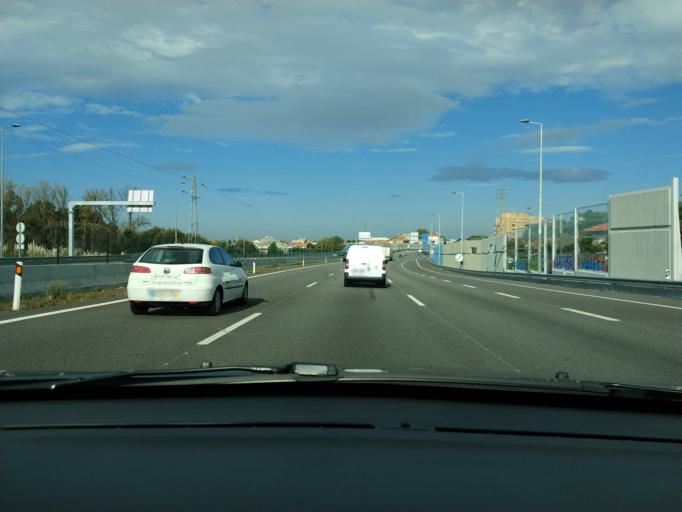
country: PT
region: Porto
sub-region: Vila Nova de Gaia
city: Vilar de Andorinho
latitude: 41.1024
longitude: -8.6002
